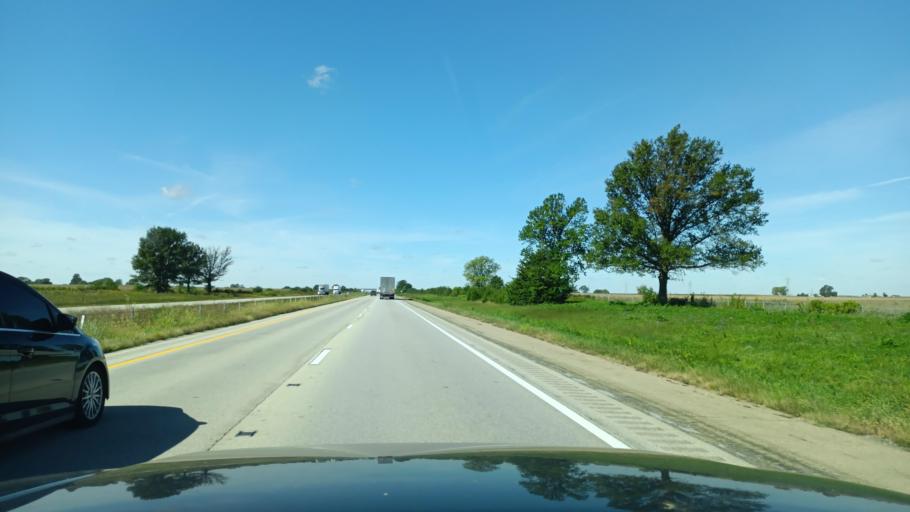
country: US
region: Illinois
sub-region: Vermilion County
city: Oakwood
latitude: 40.1253
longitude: -87.8603
